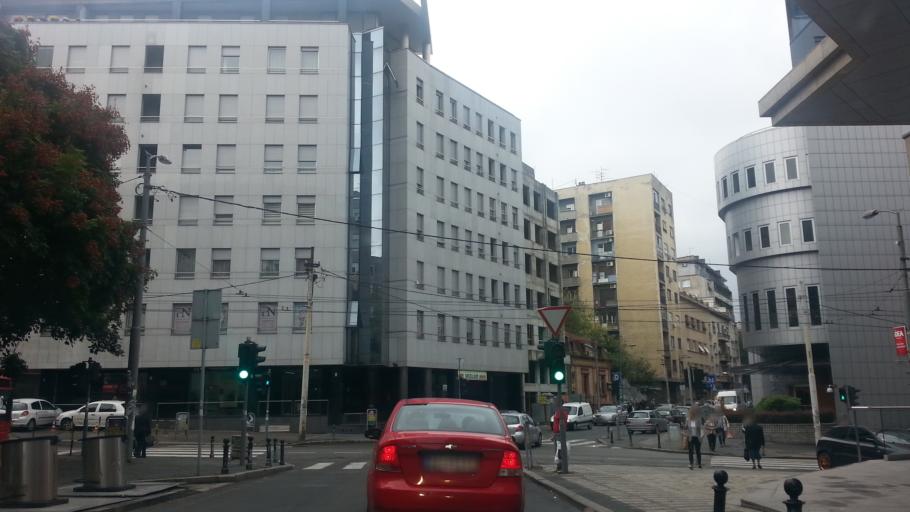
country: RS
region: Central Serbia
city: Belgrade
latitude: 44.8012
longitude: 20.4700
